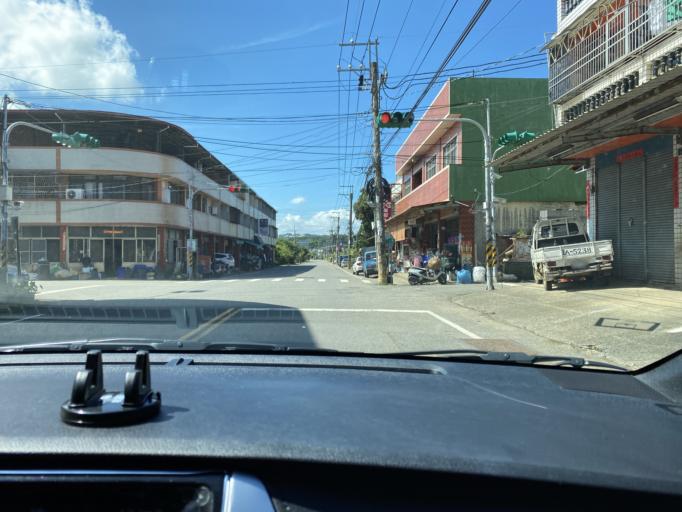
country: TW
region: Taiwan
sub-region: Nantou
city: Nantou
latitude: 23.8736
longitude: 120.6331
